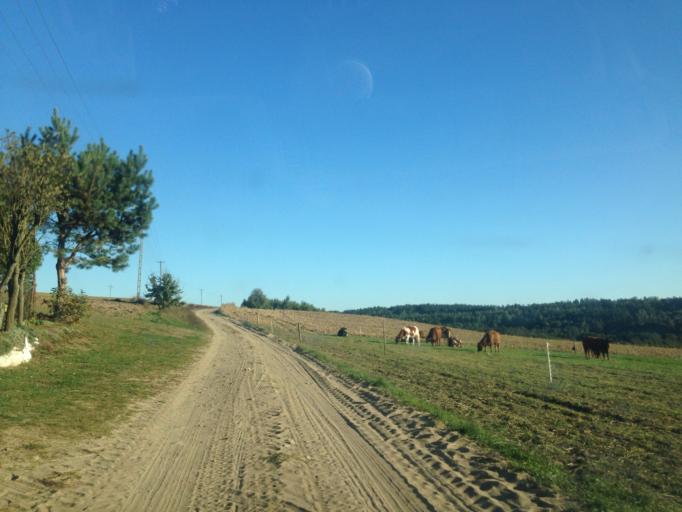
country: PL
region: Kujawsko-Pomorskie
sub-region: Powiat brodnicki
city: Bartniczka
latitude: 53.2789
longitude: 19.5991
